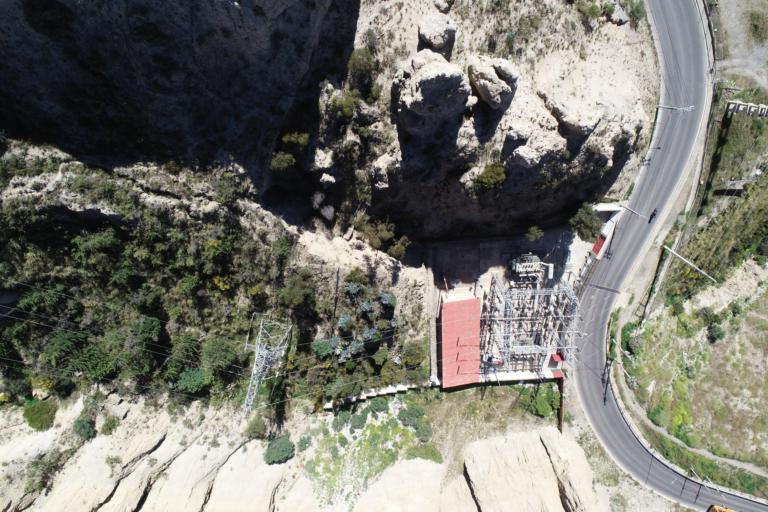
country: BO
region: La Paz
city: La Paz
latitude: -16.5248
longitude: -68.0938
